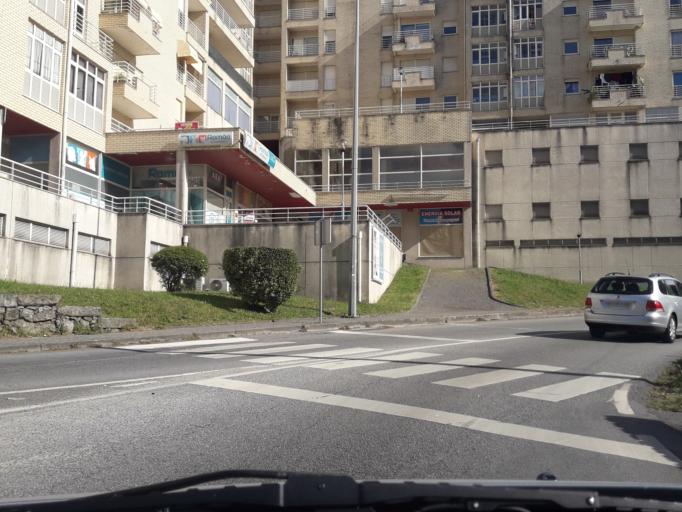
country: PT
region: Braga
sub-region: Vila Nova de Famalicao
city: Vila Nova de Famalicao
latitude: 41.4005
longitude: -8.5150
